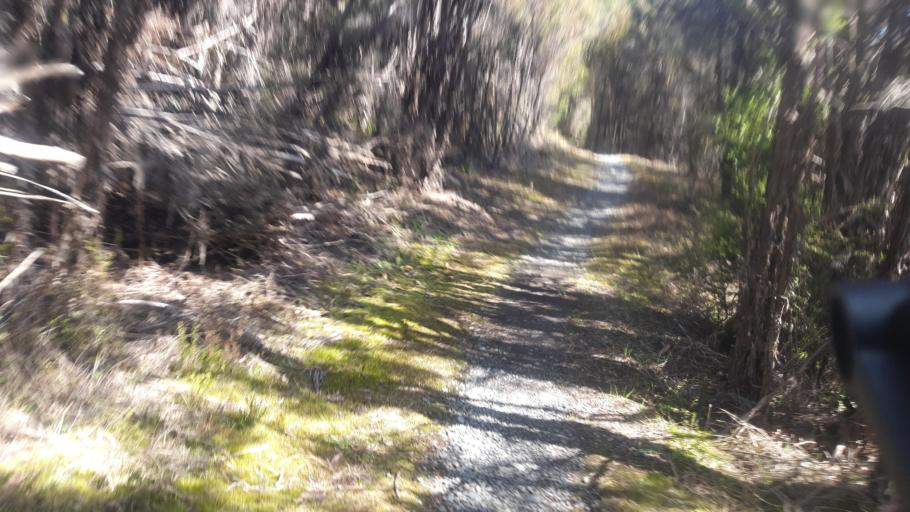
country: NZ
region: Tasman
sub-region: Tasman District
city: Wakefield
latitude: -41.8007
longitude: 172.8393
